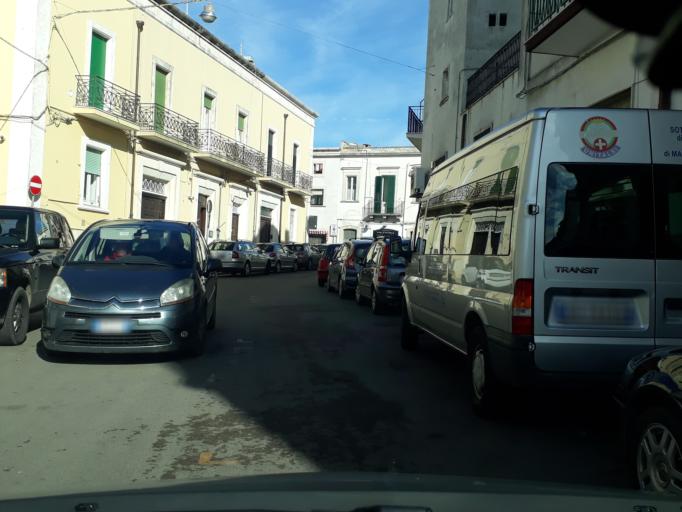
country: IT
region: Apulia
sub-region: Provincia di Taranto
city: Martina Franca
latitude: 40.7022
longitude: 17.3422
